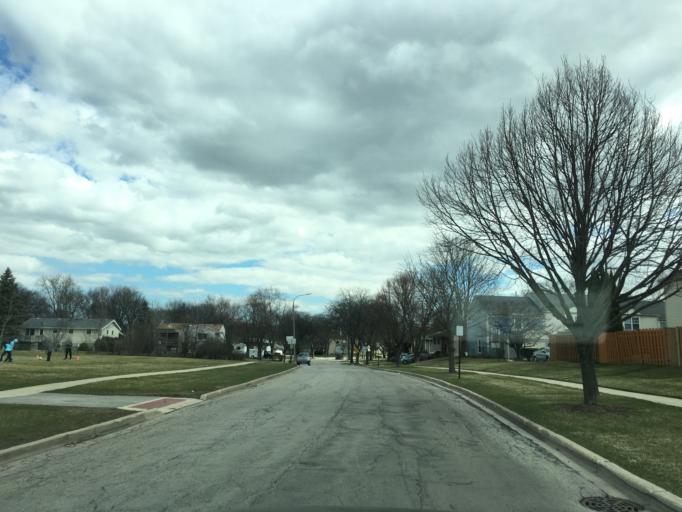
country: US
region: Illinois
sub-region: DuPage County
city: Hanover Park
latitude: 42.0076
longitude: -88.1265
